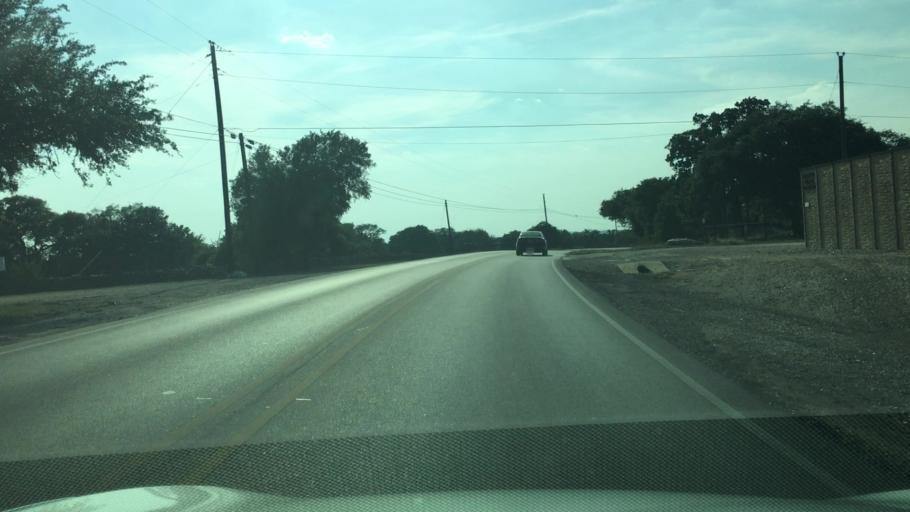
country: US
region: Texas
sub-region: Hays County
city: Dripping Springs
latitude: 30.1173
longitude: -97.9858
